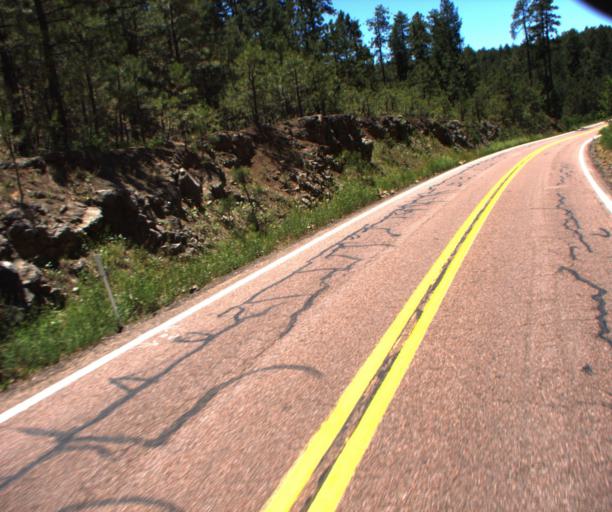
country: US
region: Arizona
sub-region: Gila County
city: Pine
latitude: 34.4640
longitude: -111.3847
